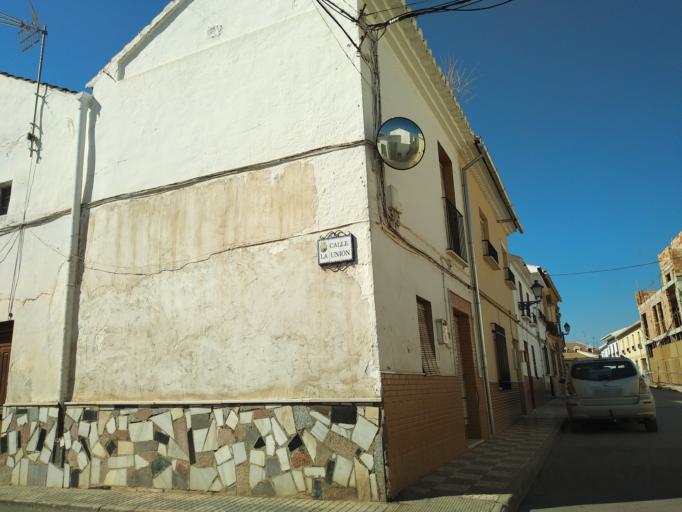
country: ES
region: Andalusia
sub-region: Provincia de Malaga
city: Mollina
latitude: 37.1291
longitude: -4.6573
